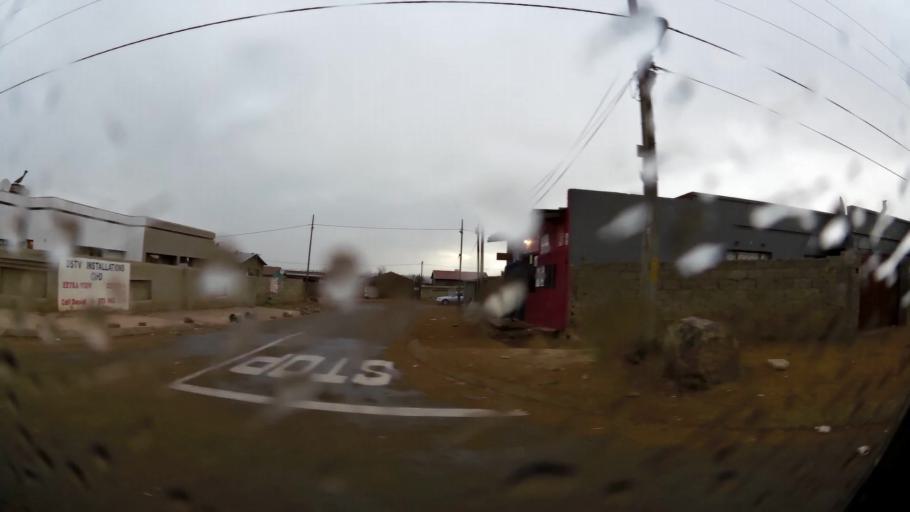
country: ZA
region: Gauteng
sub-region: City of Johannesburg Metropolitan Municipality
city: Roodepoort
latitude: -26.1766
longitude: 27.7908
